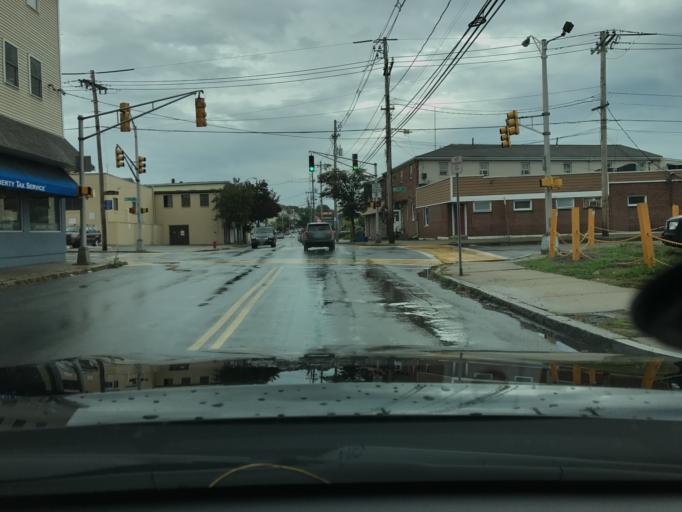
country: US
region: Massachusetts
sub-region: Essex County
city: Peabody
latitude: 42.5267
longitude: -70.9248
